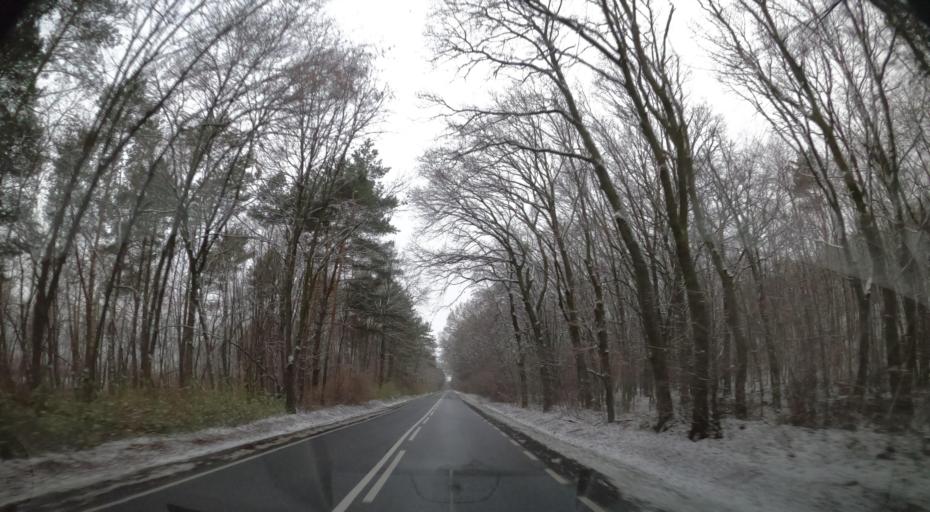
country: PL
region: Masovian Voivodeship
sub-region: Powiat plocki
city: Maszewo Duze
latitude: 52.5734
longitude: 19.5593
